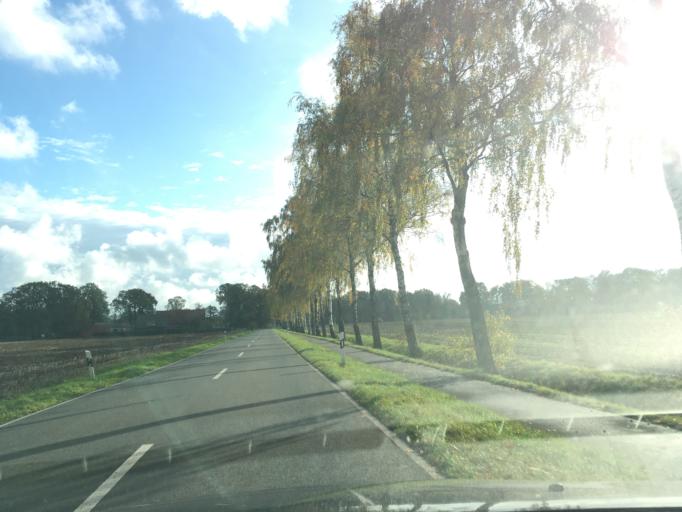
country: DE
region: North Rhine-Westphalia
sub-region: Regierungsbezirk Munster
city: Vreden
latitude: 52.0958
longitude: 6.8645
